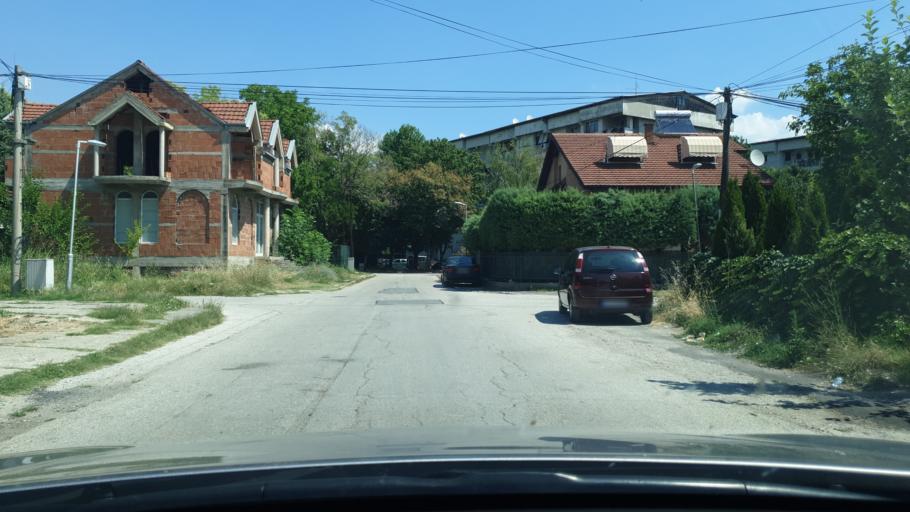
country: MK
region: Kisela Voda
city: Kisela Voda
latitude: 41.9425
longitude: 21.5176
